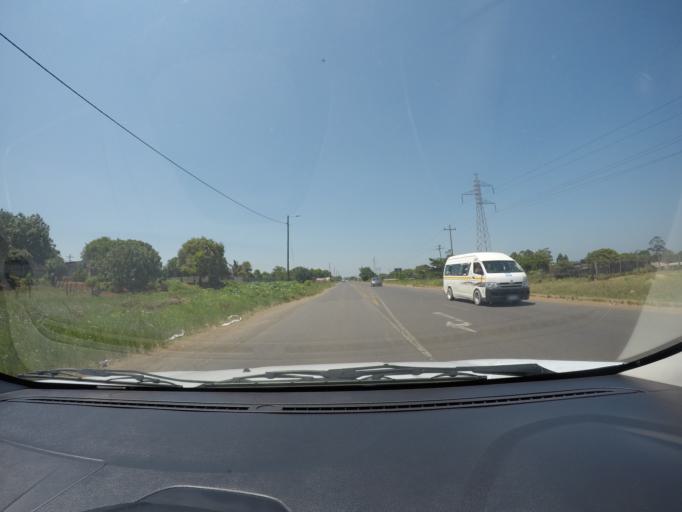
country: ZA
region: KwaZulu-Natal
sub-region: uThungulu District Municipality
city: eSikhawini
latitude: -28.8409
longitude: 31.9351
